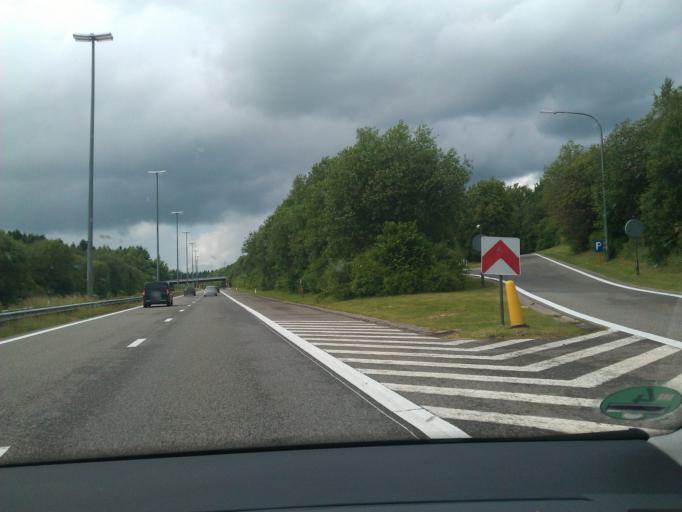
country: BE
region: Wallonia
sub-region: Province de Liege
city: Saint-Vith
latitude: 50.2506
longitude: 6.1716
